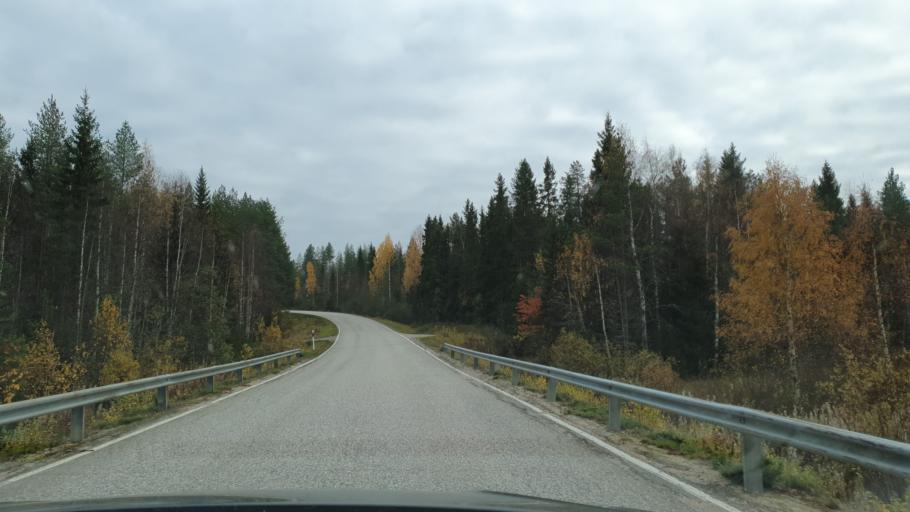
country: FI
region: Kainuu
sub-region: Kajaani
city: Ristijaervi
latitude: 64.4726
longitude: 28.2899
